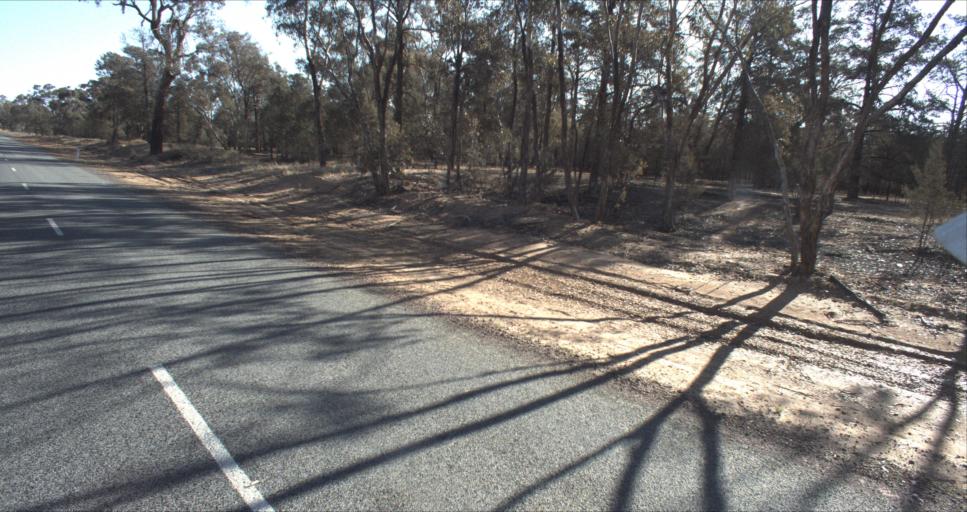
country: AU
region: New South Wales
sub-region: Leeton
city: Leeton
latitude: -34.6506
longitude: 146.3513
